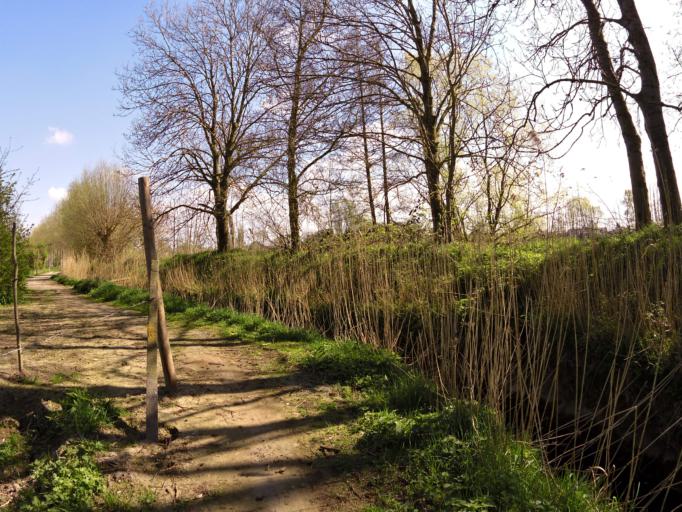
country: BE
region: Flanders
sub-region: Provincie West-Vlaanderen
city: Ichtegem
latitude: 51.1289
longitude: 3.0063
